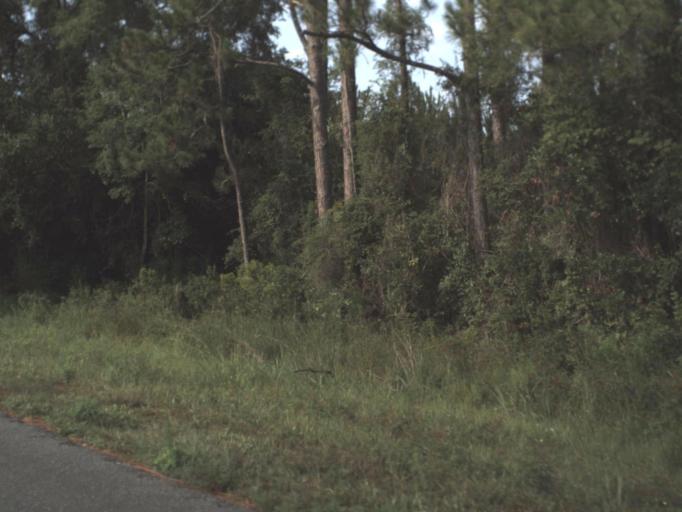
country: US
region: Florida
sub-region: Taylor County
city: Perry
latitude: 30.2034
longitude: -83.6074
